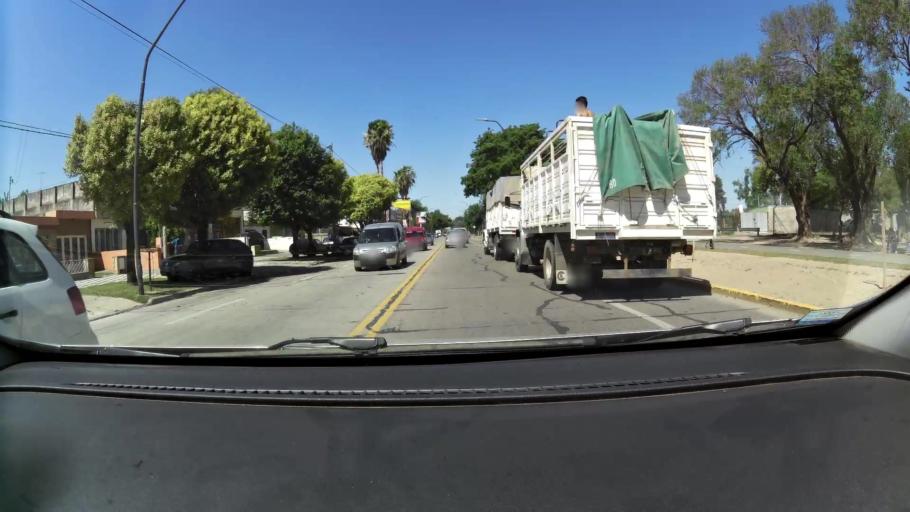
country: AR
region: Cordoba
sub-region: Departamento de Capital
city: Cordoba
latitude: -31.3795
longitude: -64.1440
